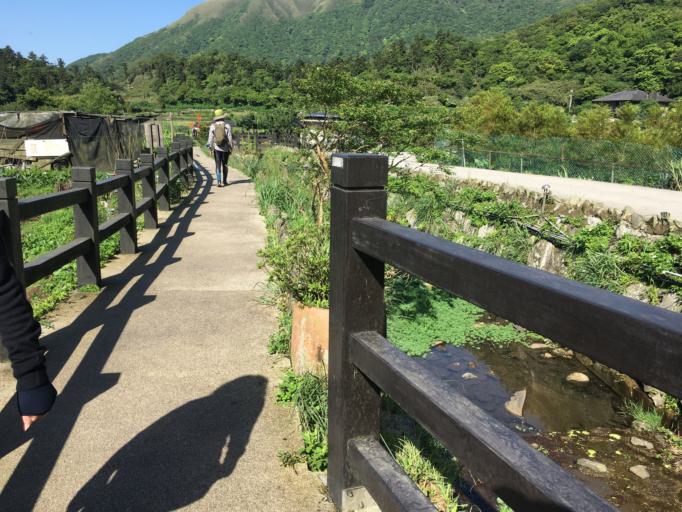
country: TW
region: Taipei
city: Taipei
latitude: 25.1782
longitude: 121.5402
